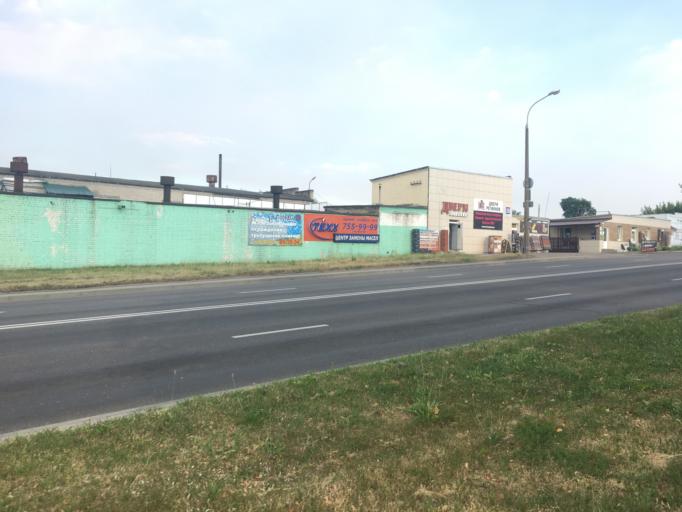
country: BY
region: Grodnenskaya
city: Hrodna
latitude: 53.6569
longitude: 23.8305
